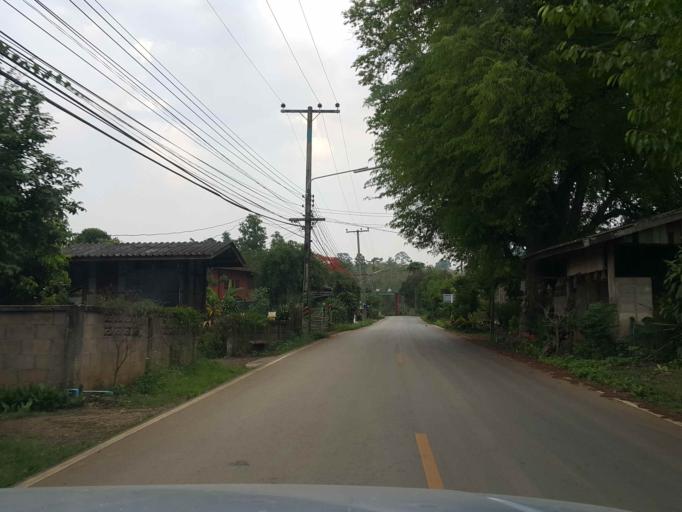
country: TH
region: Chiang Mai
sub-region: Amphoe Chiang Dao
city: Chiang Dao
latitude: 19.3863
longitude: 98.9318
